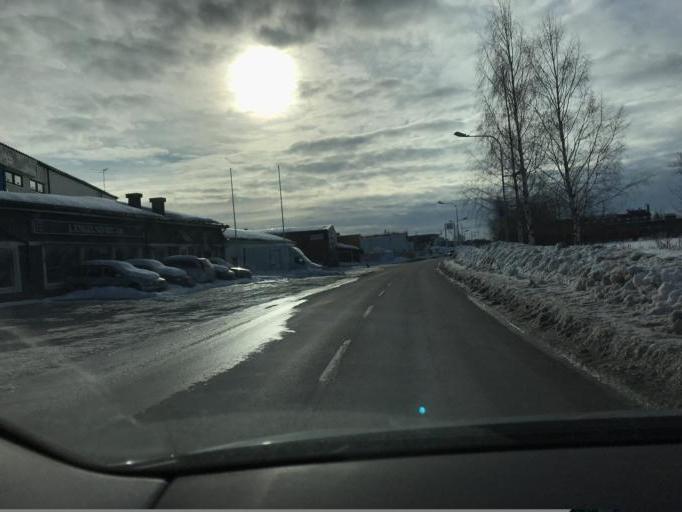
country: SE
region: Norrbotten
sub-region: Lulea Kommun
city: Lulea
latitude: 65.6066
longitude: 22.1303
